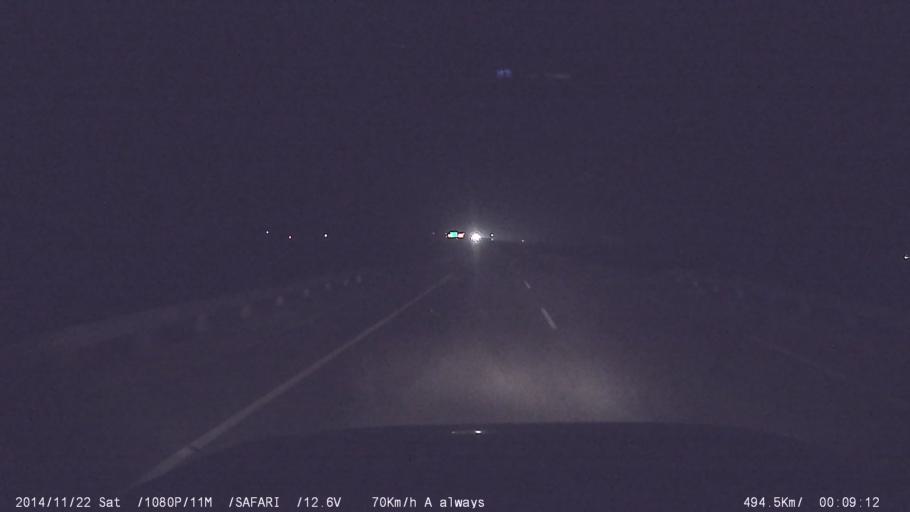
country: IN
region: Tamil Nadu
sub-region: Villupuram
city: Kallakkurichchi
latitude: 11.7386
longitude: 79.0580
